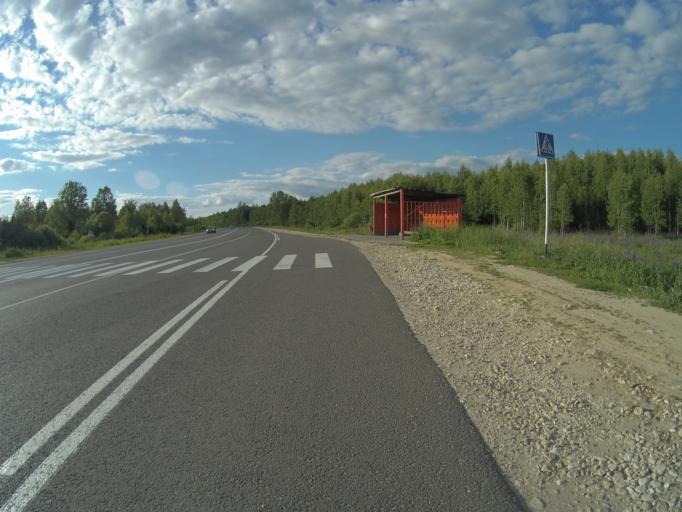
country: RU
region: Vladimir
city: Anopino
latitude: 55.7938
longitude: 40.6828
